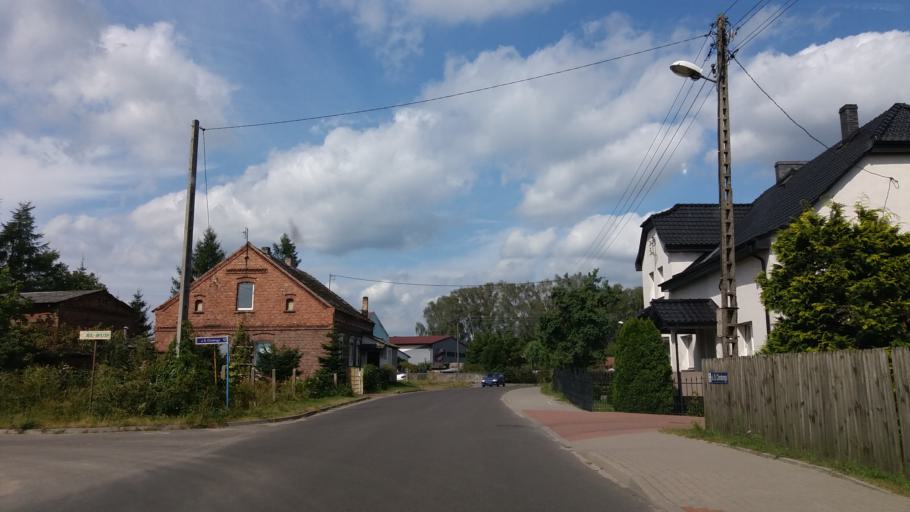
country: PL
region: West Pomeranian Voivodeship
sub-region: Powiat stargardzki
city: Kobylanka
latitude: 53.3490
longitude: 14.8683
